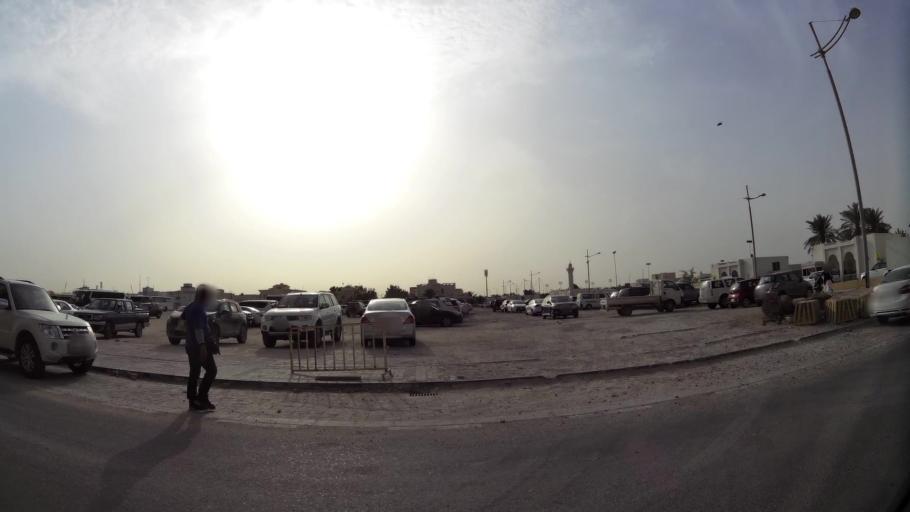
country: QA
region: Baladiyat ad Dawhah
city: Doha
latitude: 25.3253
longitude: 51.5220
